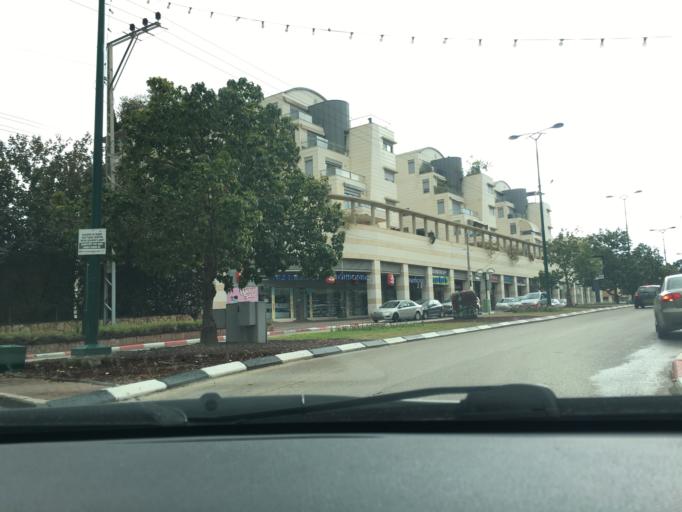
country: IL
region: Tel Aviv
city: Ramat HaSharon
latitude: 32.1439
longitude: 34.8439
